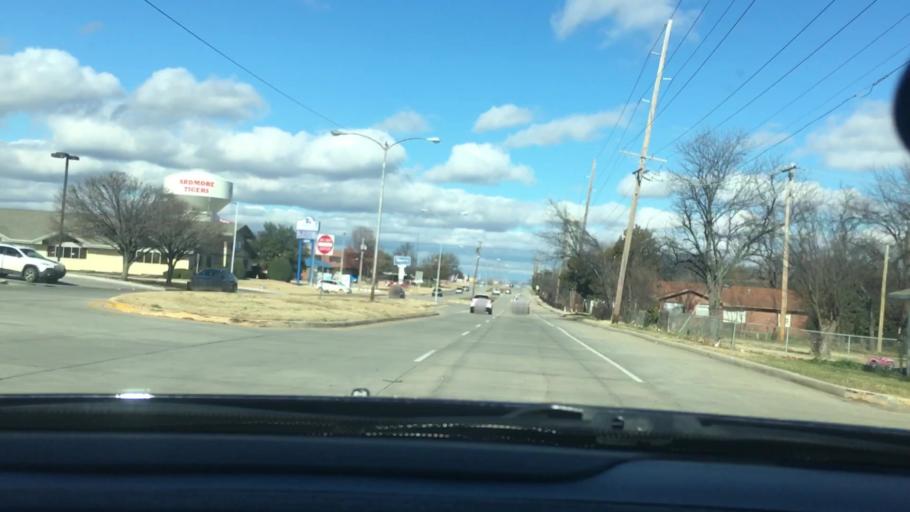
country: US
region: Oklahoma
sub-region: Carter County
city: Ardmore
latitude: 34.1938
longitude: -97.1430
